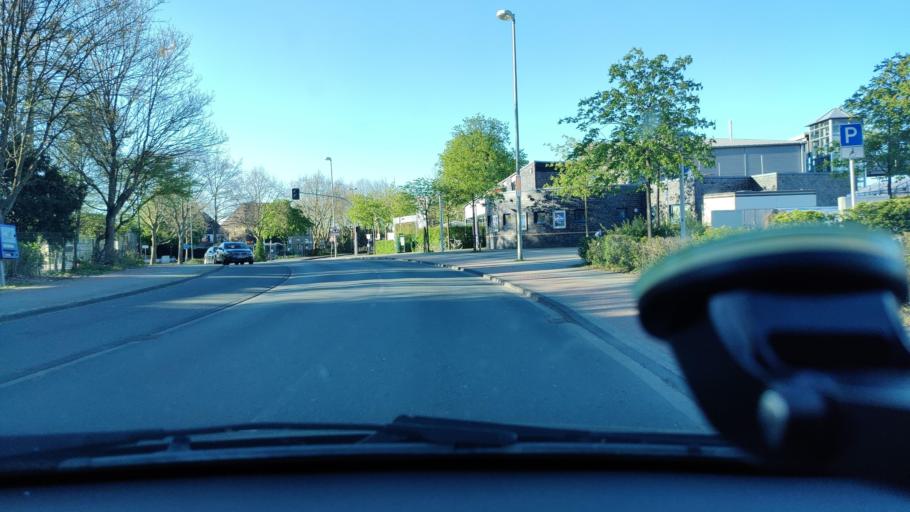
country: DE
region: North Rhine-Westphalia
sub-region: Regierungsbezirk Munster
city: Ahaus
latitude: 52.0816
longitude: 7.0160
